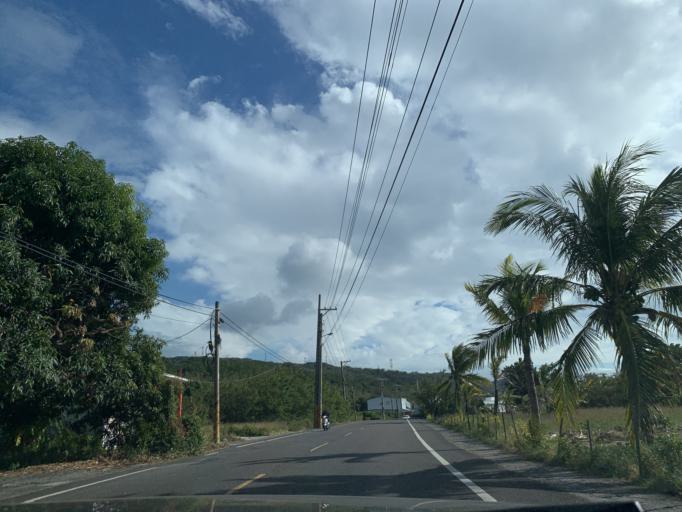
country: TW
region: Taiwan
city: Hengchun
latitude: 22.0017
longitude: 120.7534
